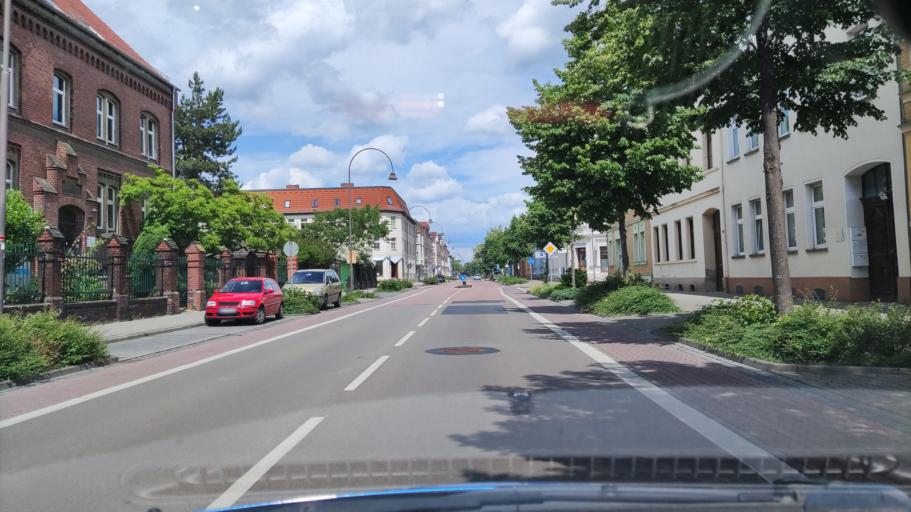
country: DE
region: Saxony-Anhalt
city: Wittenburg
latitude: 51.8704
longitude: 12.6535
